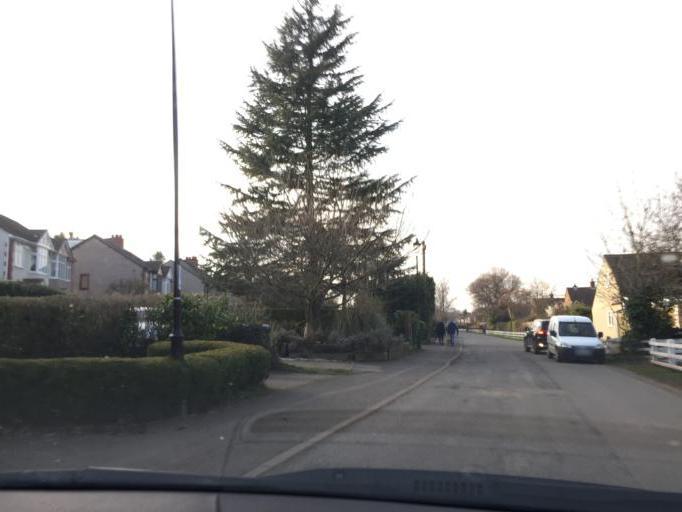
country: GB
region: England
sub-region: Coventry
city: Keresley
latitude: 52.4293
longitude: -1.5659
